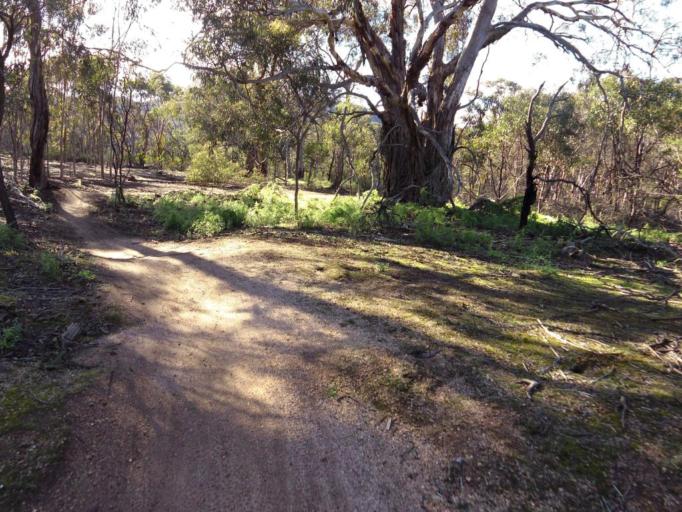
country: AU
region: Victoria
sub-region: Greater Geelong
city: Lara
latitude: -37.9623
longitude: 144.4095
